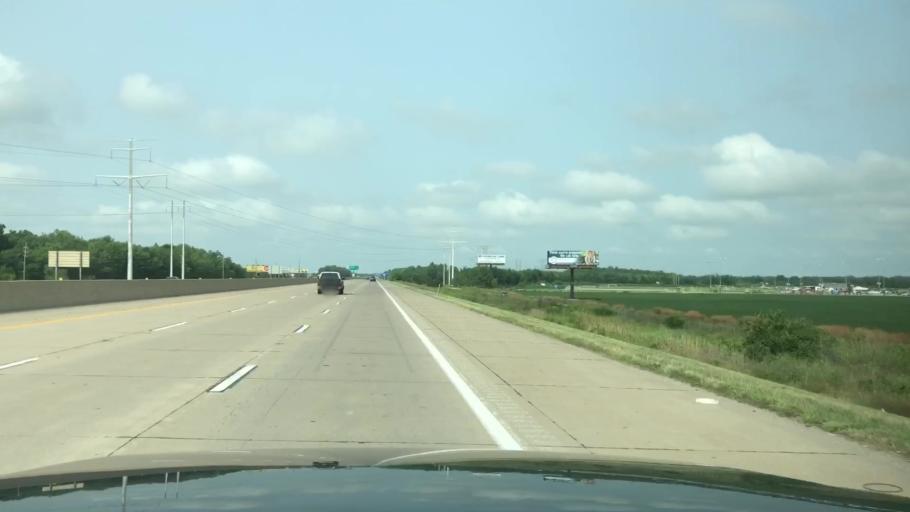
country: US
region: Missouri
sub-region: Saint Charles County
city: Saint Charles
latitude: 38.8243
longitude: -90.5341
